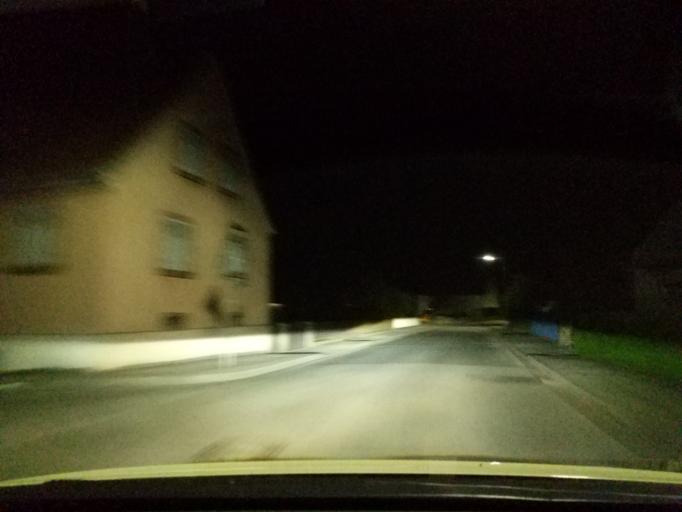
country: DE
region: Rheinland-Pfalz
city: Katzweiler
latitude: 49.4981
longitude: 7.6981
